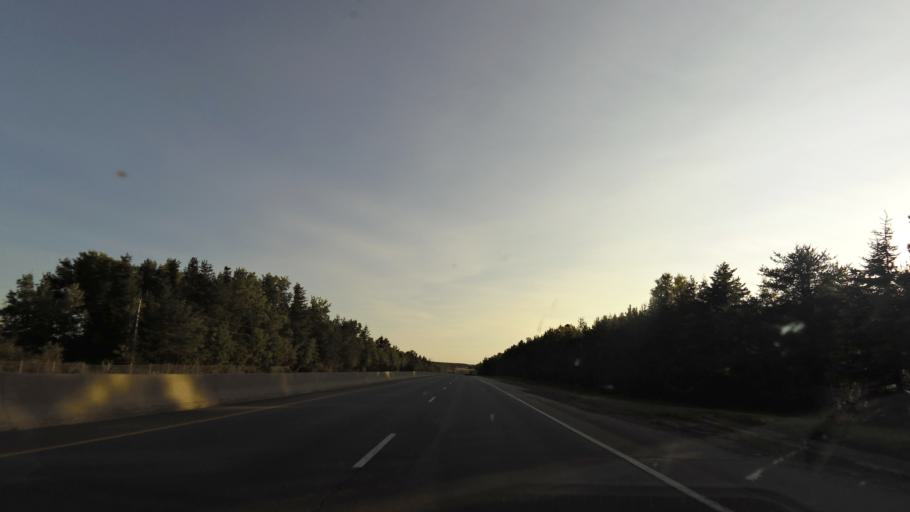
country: CA
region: New Brunswick
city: Salisbury
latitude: 45.9265
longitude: -65.1723
